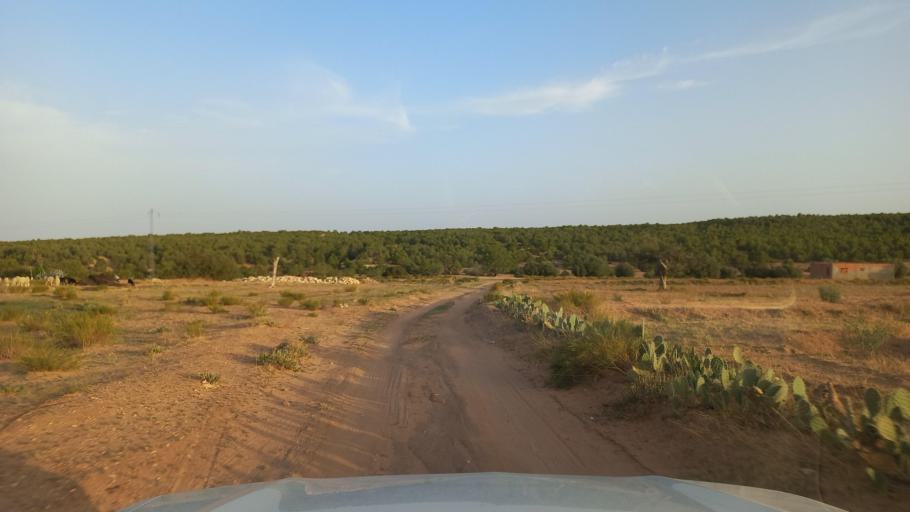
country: TN
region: Al Qasrayn
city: Sbiba
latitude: 35.4097
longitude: 8.9144
